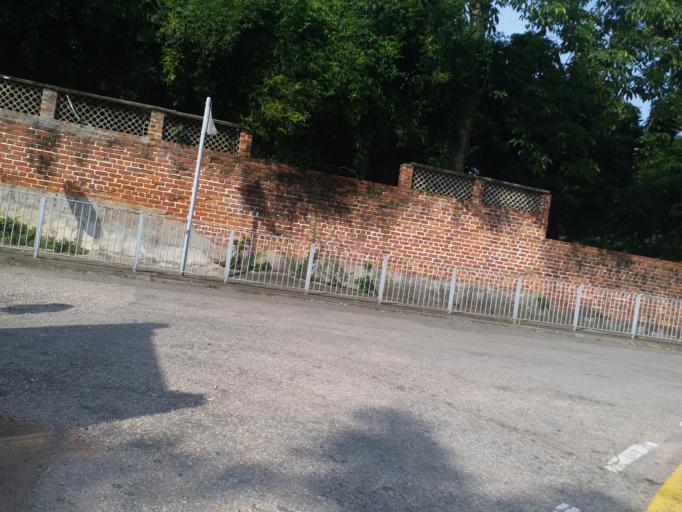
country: HK
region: Yuen Long
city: Yuen Long Kau Hui
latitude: 22.4436
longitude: 114.0105
